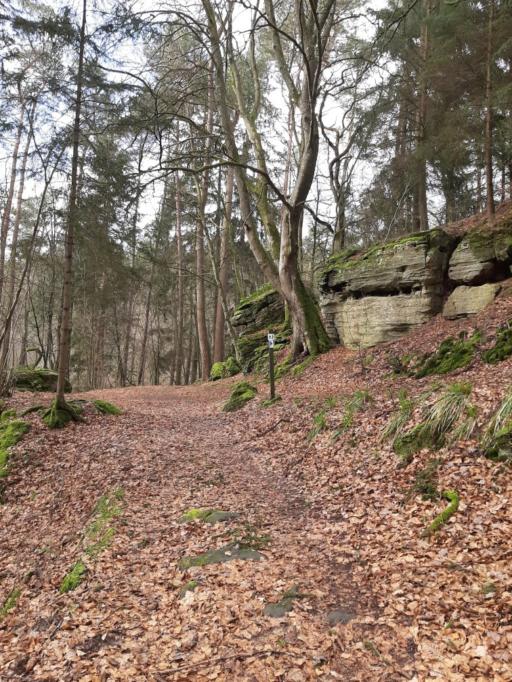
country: LU
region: Grevenmacher
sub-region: Canton d'Echternach
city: Beaufort
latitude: 49.8241
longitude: 6.2975
